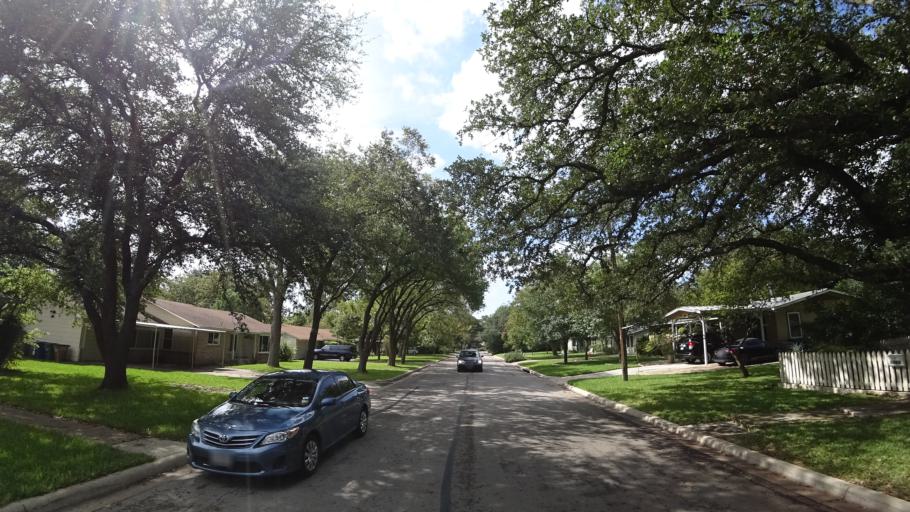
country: US
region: Texas
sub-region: Travis County
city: West Lake Hills
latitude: 30.3411
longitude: -97.7431
